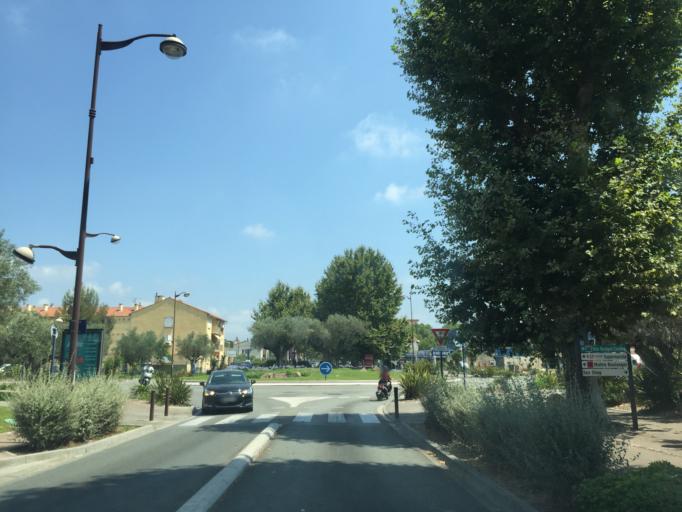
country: FR
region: Provence-Alpes-Cote d'Azur
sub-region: Departement du Var
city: Frejus
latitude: 43.4325
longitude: 6.7489
